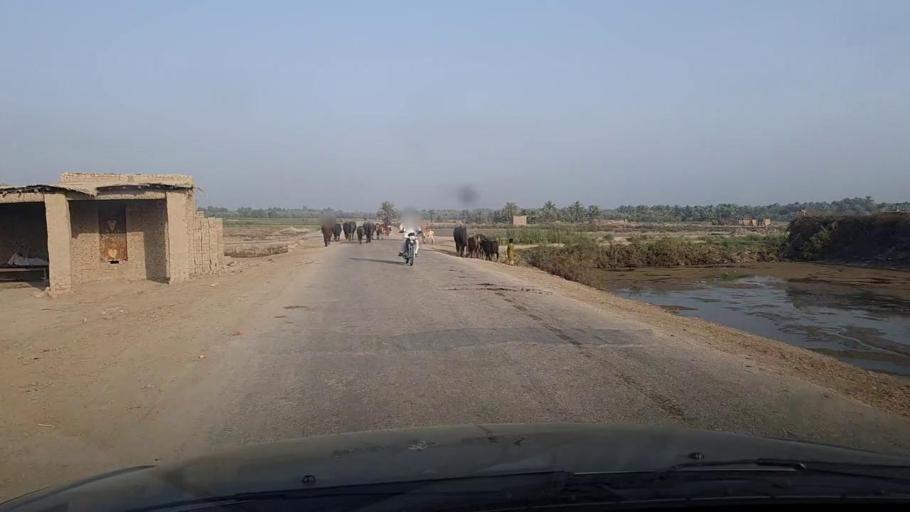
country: PK
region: Sindh
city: Khairpur
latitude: 27.5498
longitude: 68.6926
